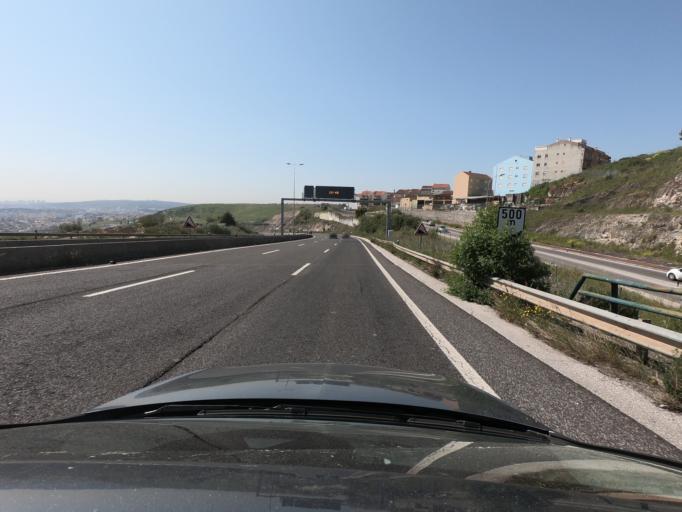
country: PT
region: Lisbon
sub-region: Odivelas
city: Famoes
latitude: 38.7817
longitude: -9.2293
